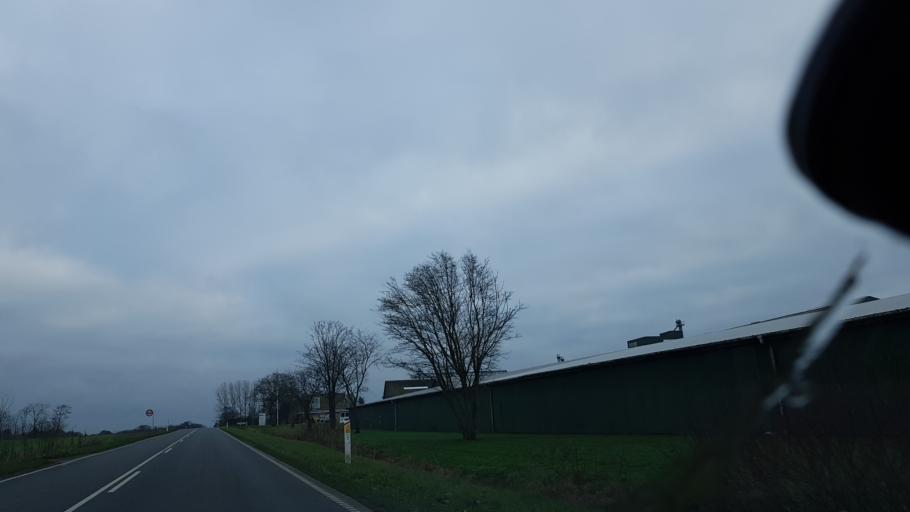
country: DK
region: South Denmark
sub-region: Tonder Kommune
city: Toftlund
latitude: 55.1935
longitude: 9.0831
